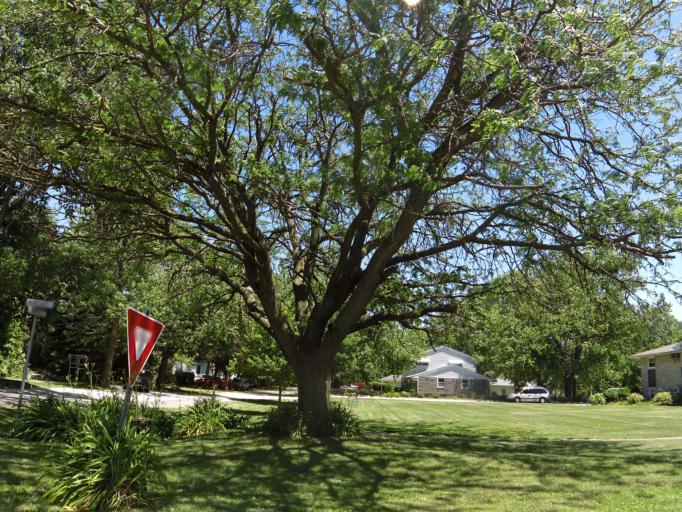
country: US
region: Illinois
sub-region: Livingston County
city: Chatsworth
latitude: 40.7571
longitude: -88.1884
